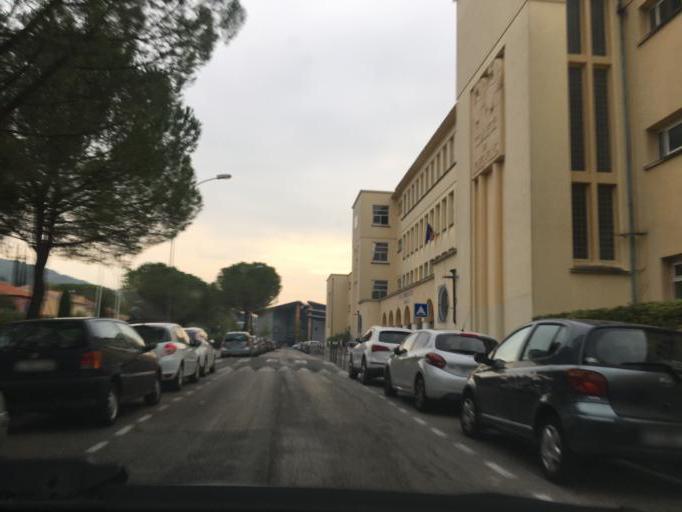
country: FR
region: Provence-Alpes-Cote d'Azur
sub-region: Departement du Var
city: Draguignan
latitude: 43.5353
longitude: 6.4705
